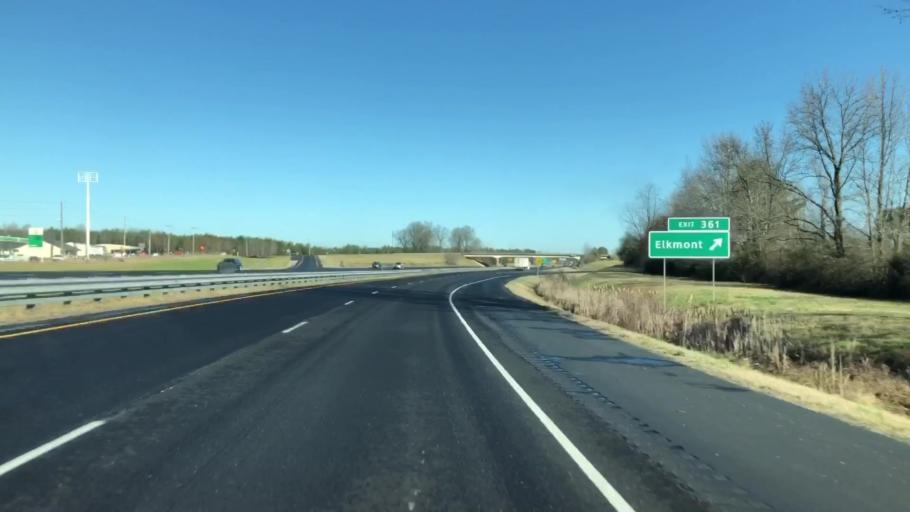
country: US
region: Alabama
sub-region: Limestone County
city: Ardmore
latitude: 34.9162
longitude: -86.9085
